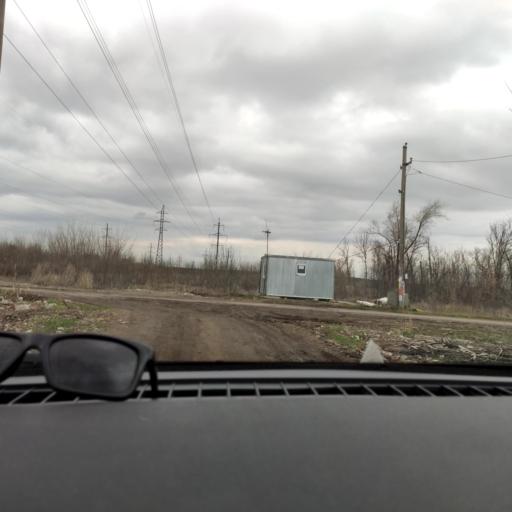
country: RU
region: Samara
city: Dubovyy Umet
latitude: 53.0938
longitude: 50.2335
